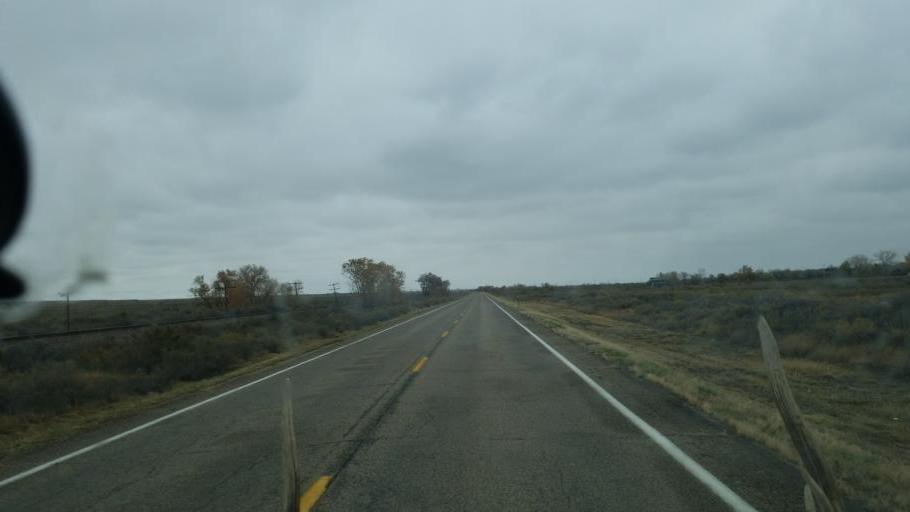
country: US
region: Colorado
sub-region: Pueblo County
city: Pueblo
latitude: 38.2547
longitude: -104.3091
